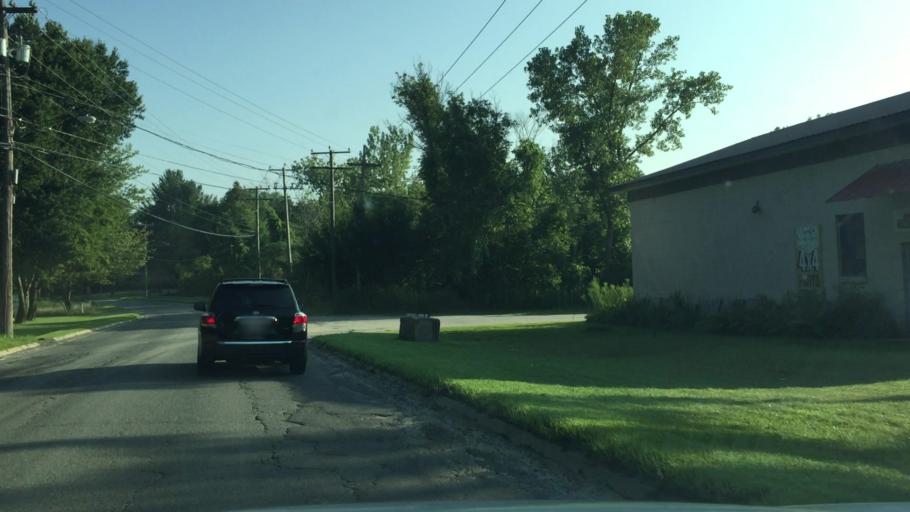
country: US
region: Massachusetts
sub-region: Berkshire County
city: Dalton
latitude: 42.4608
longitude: -73.1888
